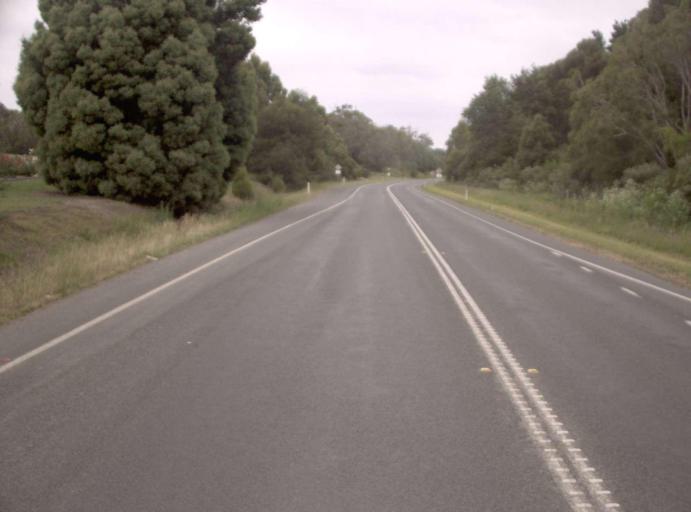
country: AU
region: Victoria
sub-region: Bass Coast
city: North Wonthaggi
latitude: -38.5360
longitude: 145.9502
